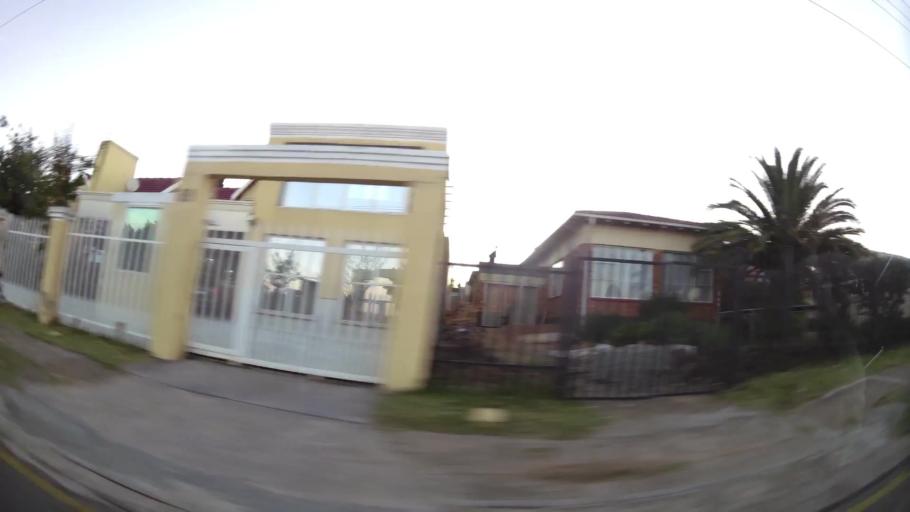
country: ZA
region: Gauteng
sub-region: City of Johannesburg Metropolitan Municipality
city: Roodepoort
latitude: -26.1576
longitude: 27.9004
